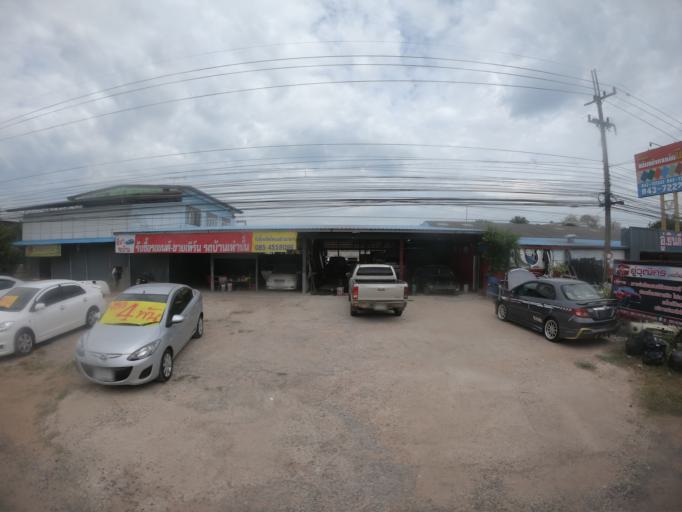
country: TH
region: Maha Sarakham
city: Maha Sarakham
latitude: 16.1657
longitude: 103.3324
